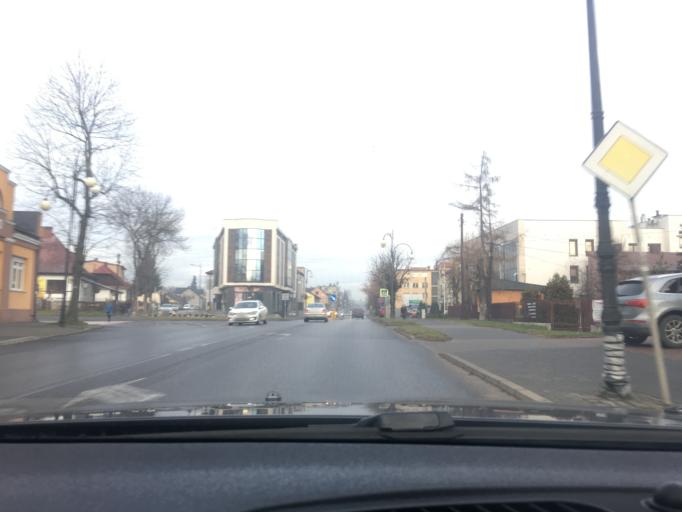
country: PL
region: Swietokrzyskie
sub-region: Powiat jedrzejowski
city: Jedrzejow
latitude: 50.6434
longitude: 20.2972
